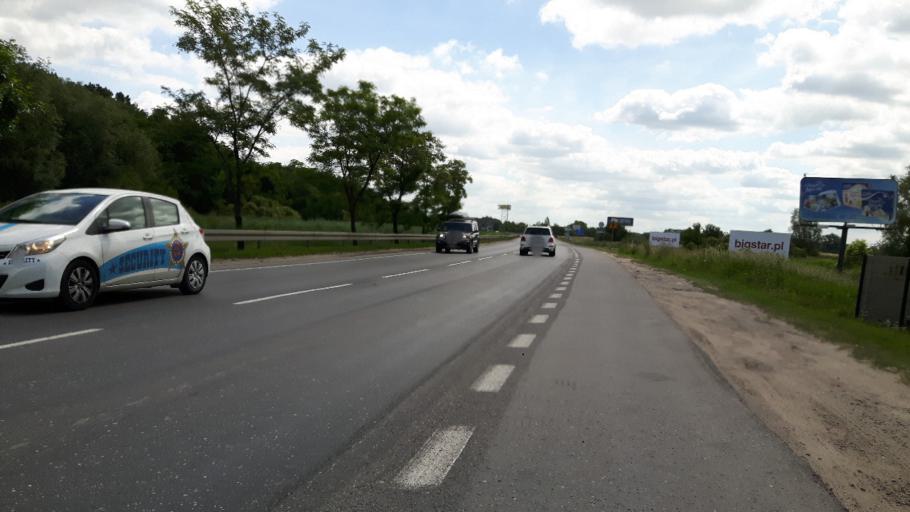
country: PL
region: Pomeranian Voivodeship
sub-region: Gdansk
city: Gdansk
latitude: 54.3421
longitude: 18.7259
